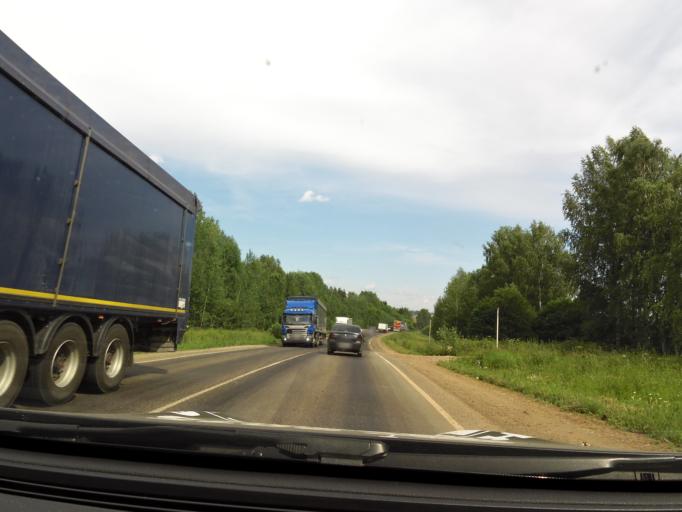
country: RU
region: Kirov
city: Vakhrushi
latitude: 58.6782
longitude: 49.9905
